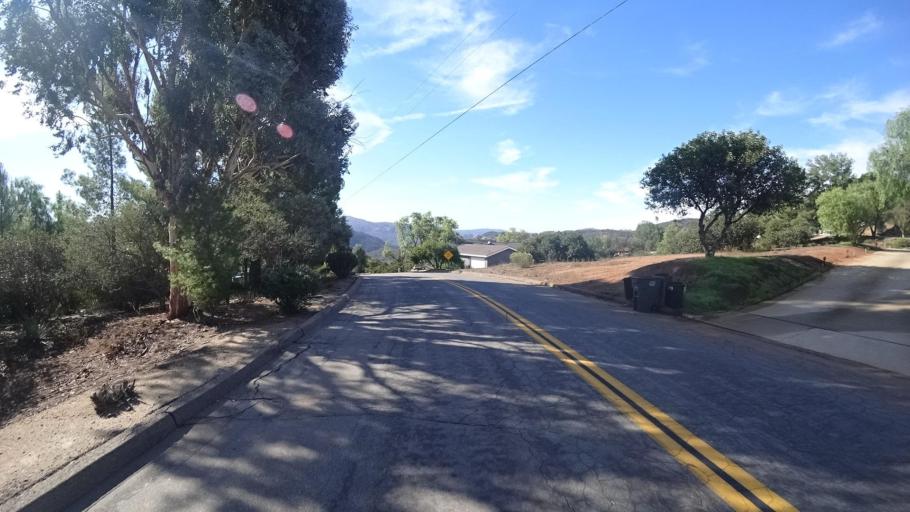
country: US
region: California
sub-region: San Diego County
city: Alpine
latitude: 32.8209
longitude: -116.7423
